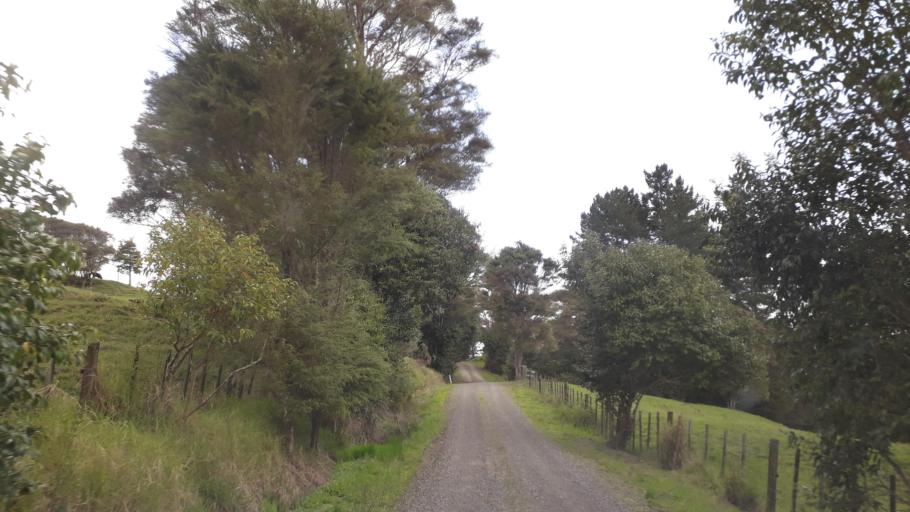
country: NZ
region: Northland
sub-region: Far North District
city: Waimate North
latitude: -35.3159
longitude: 173.5731
